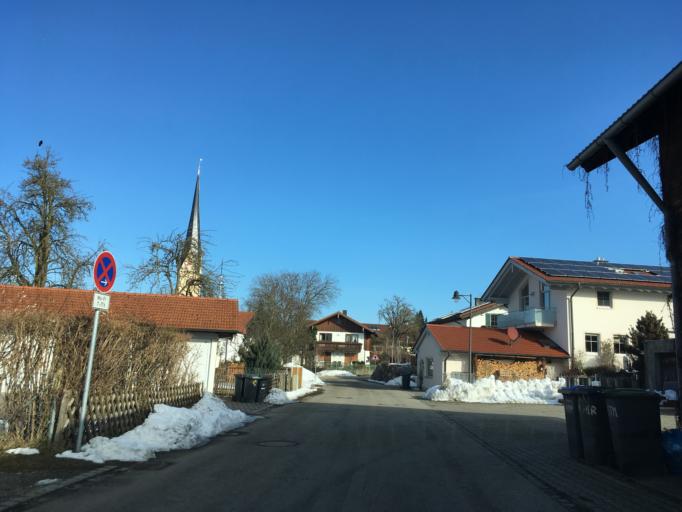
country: DE
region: Bavaria
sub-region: Upper Bavaria
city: Schechen
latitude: 47.9024
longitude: 12.1478
